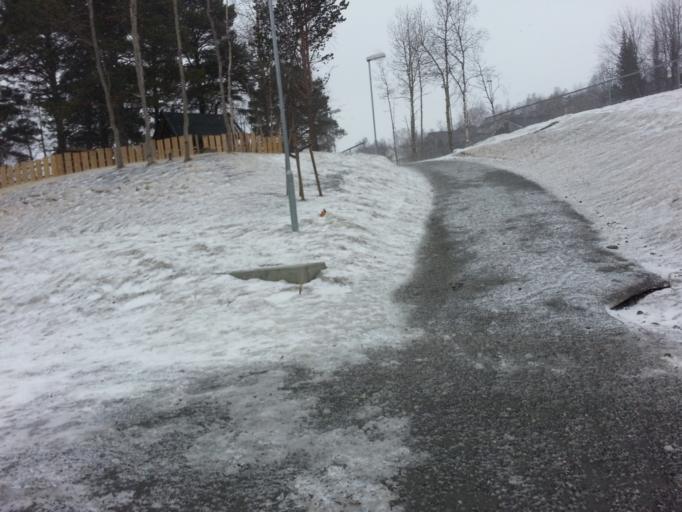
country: NO
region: Sor-Trondelag
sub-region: Oppdal
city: Oppdal
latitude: 62.5971
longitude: 9.6834
